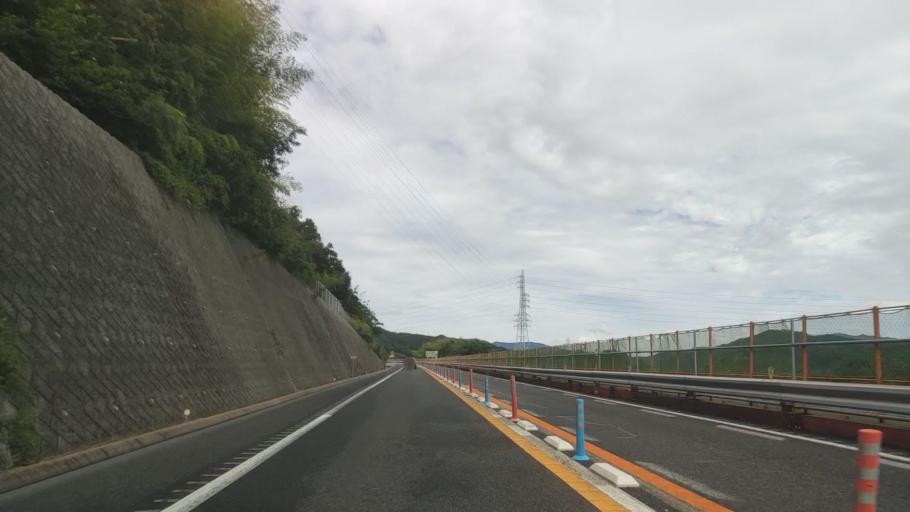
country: JP
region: Wakayama
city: Gobo
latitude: 33.8347
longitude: 135.2203
